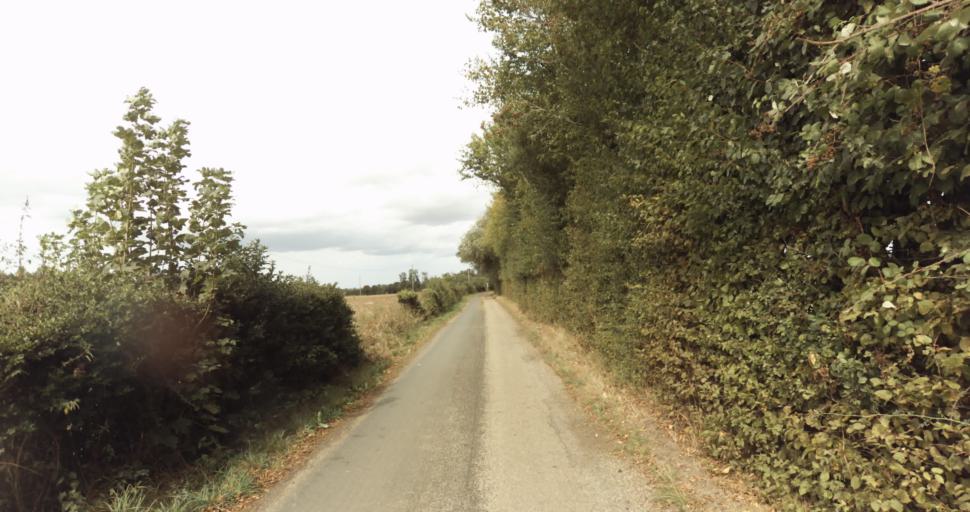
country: FR
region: Lower Normandy
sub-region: Departement de l'Orne
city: Gace
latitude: 48.8827
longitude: 0.3609
